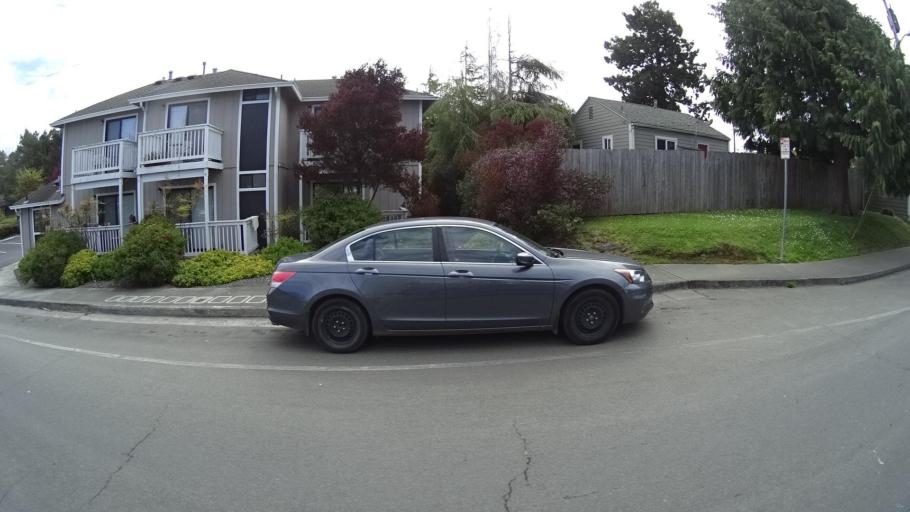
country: US
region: California
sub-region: Humboldt County
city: Arcata
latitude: 40.8774
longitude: -124.0837
